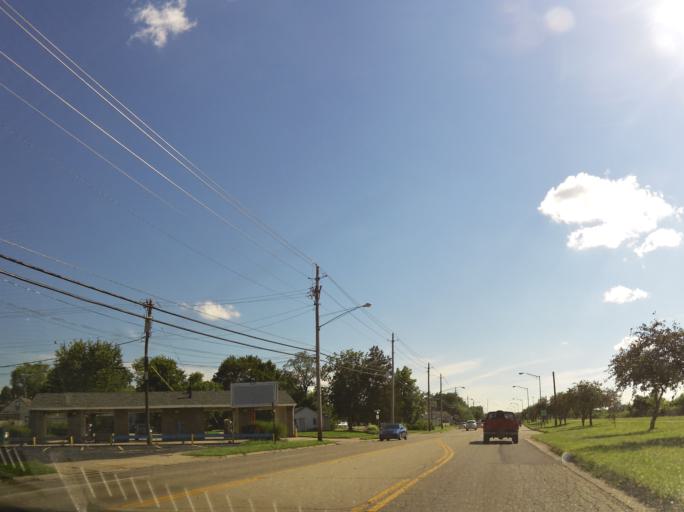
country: US
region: Ohio
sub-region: Greene County
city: Fairborn
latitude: 39.8056
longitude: -84.0313
